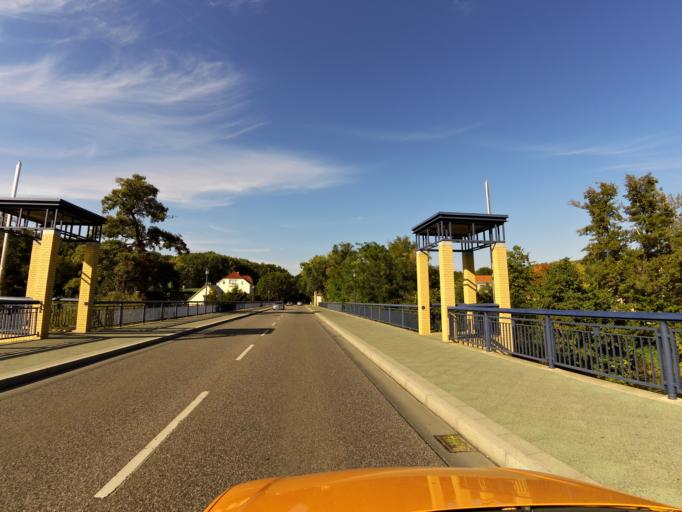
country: DE
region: Brandenburg
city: Potsdam
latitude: 52.4414
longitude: 13.0484
